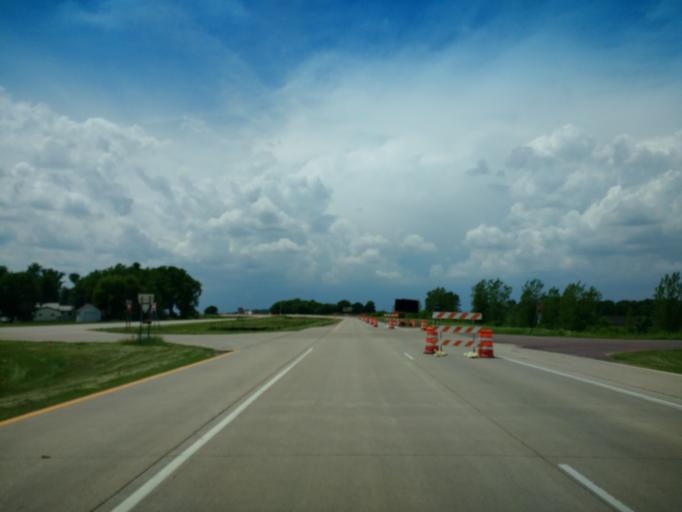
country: US
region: Minnesota
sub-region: Jackson County
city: Lakefield
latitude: 43.8004
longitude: -95.3176
